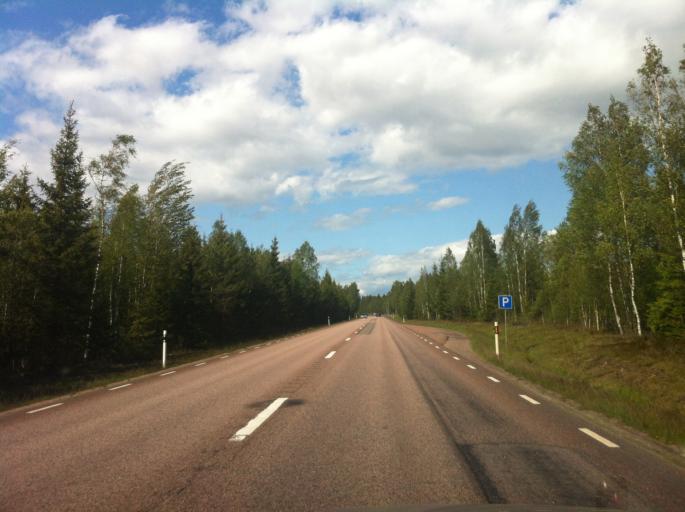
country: SE
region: Vaermland
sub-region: Kristinehamns Kommun
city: Bjorneborg
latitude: 59.1855
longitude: 14.1800
